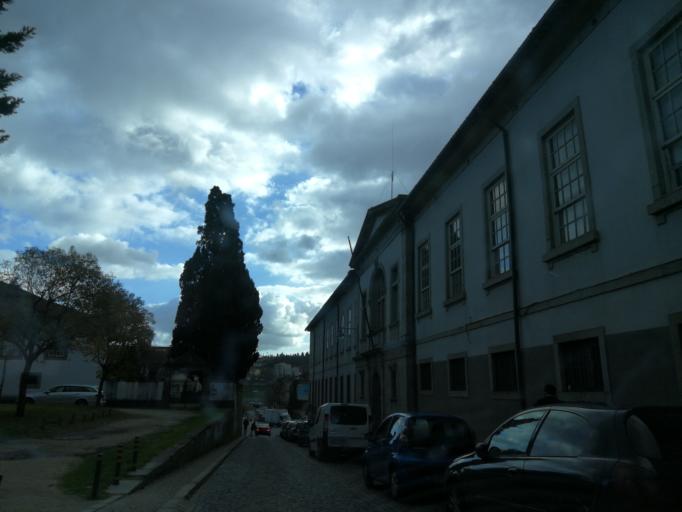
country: PT
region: Braga
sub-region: Braga
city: Braga
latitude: 41.5454
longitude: -8.4259
